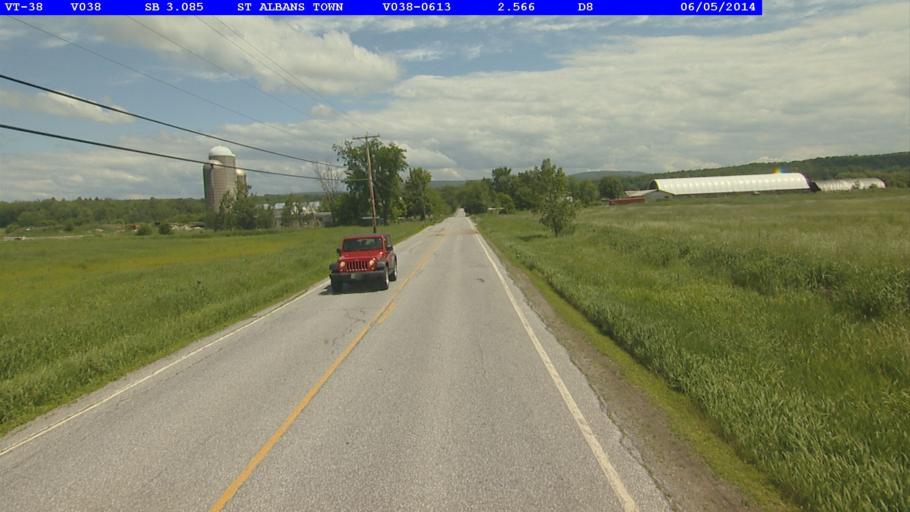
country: US
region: Vermont
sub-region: Franklin County
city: Saint Albans
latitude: 44.8504
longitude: -73.1232
